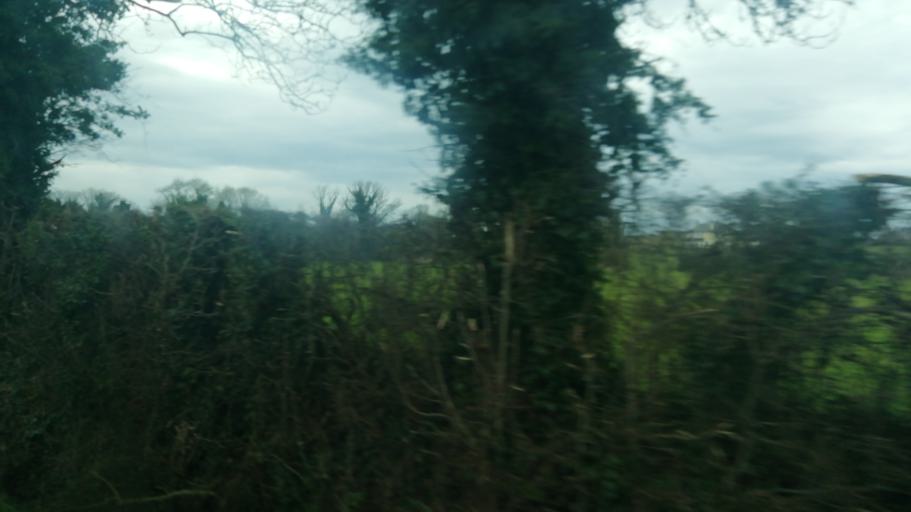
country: IE
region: Leinster
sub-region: Kildare
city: Clane
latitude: 53.3417
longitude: -6.6558
